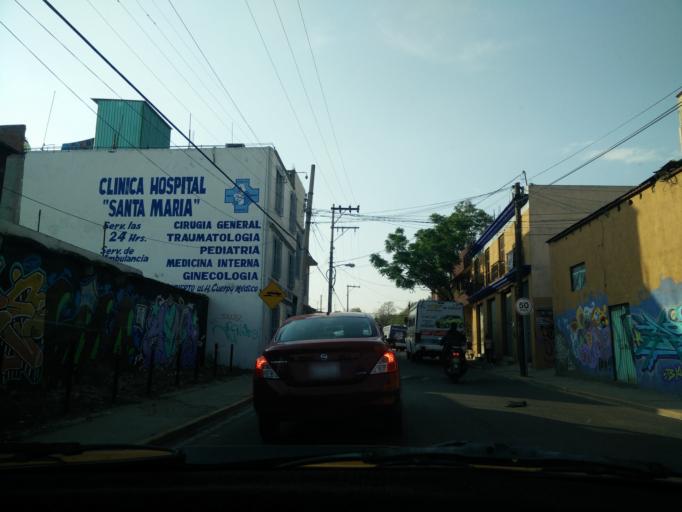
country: MX
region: Oaxaca
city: Oaxaca de Juarez
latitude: 17.0703
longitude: -96.7364
